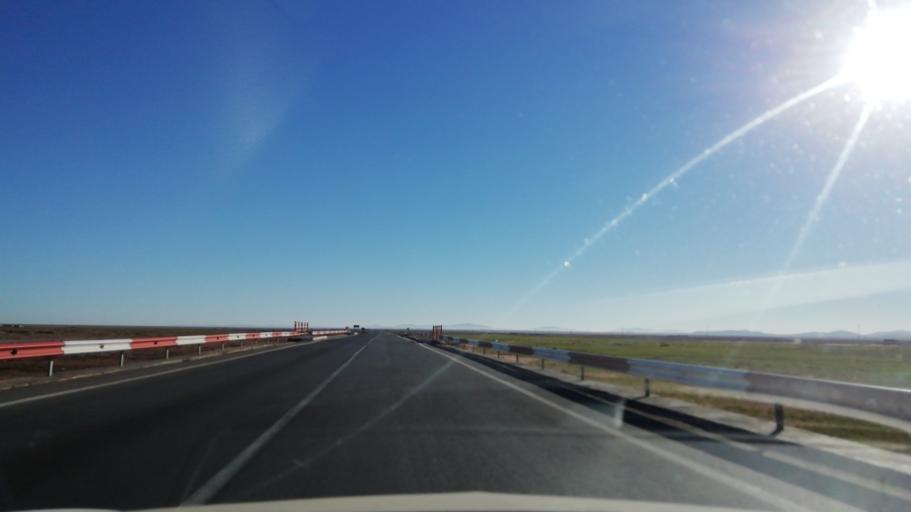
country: DZ
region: El Bayadh
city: El Bayadh
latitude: 33.8592
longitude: 0.5649
